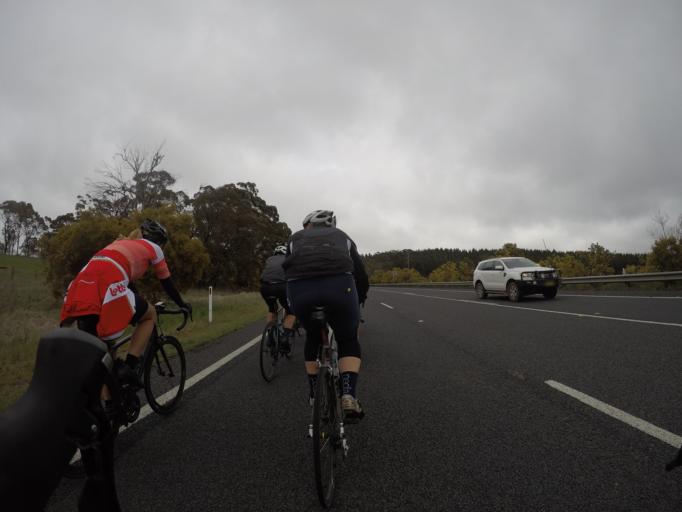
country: AU
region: New South Wales
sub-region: Lithgow
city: Portland
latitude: -33.4551
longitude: 149.9756
